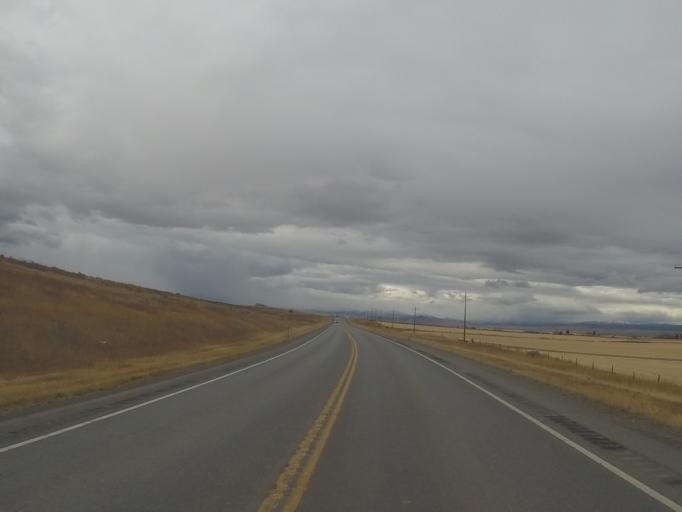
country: US
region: Montana
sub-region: Lewis and Clark County
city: East Helena
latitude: 46.5489
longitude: -111.7539
